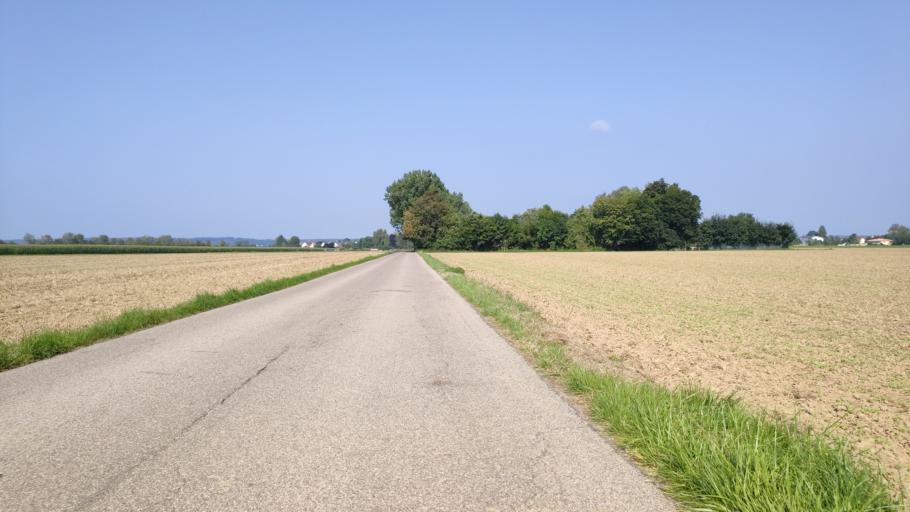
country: DE
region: Bavaria
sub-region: Swabia
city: Bobingen
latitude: 48.2581
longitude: 10.8409
